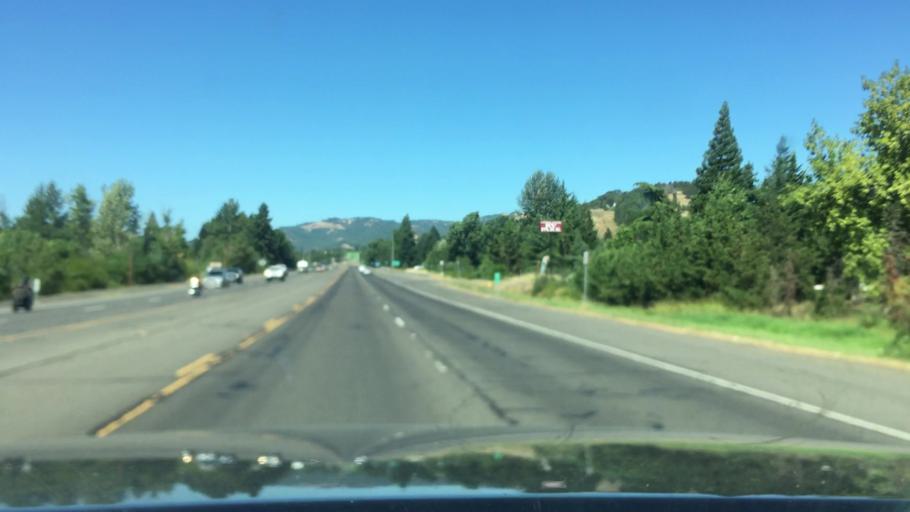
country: US
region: Oregon
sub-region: Douglas County
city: Winston
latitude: 43.1294
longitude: -123.4070
